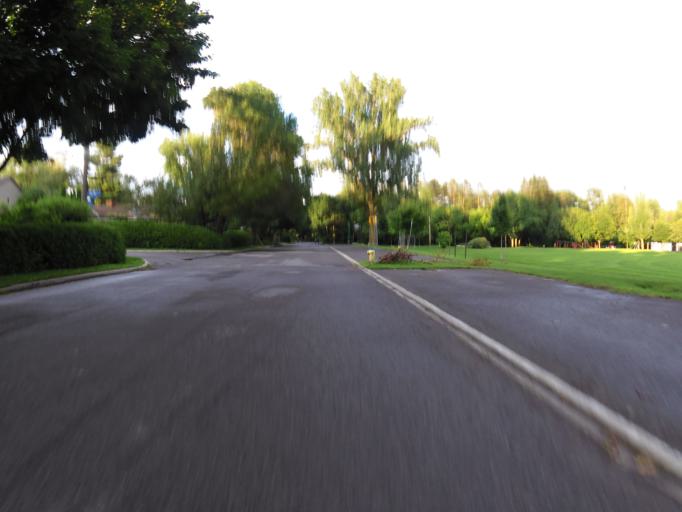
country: CA
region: Ontario
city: Bells Corners
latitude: 45.3569
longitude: -75.7911
